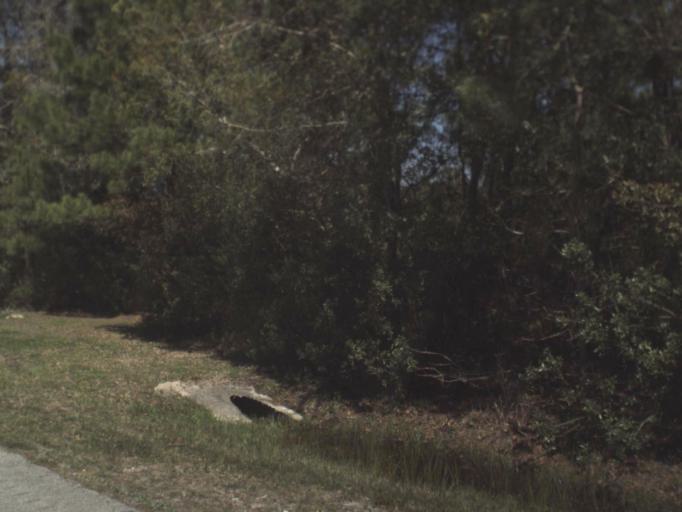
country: US
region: Florida
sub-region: Leon County
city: Woodville
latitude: 30.1678
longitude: -84.2081
